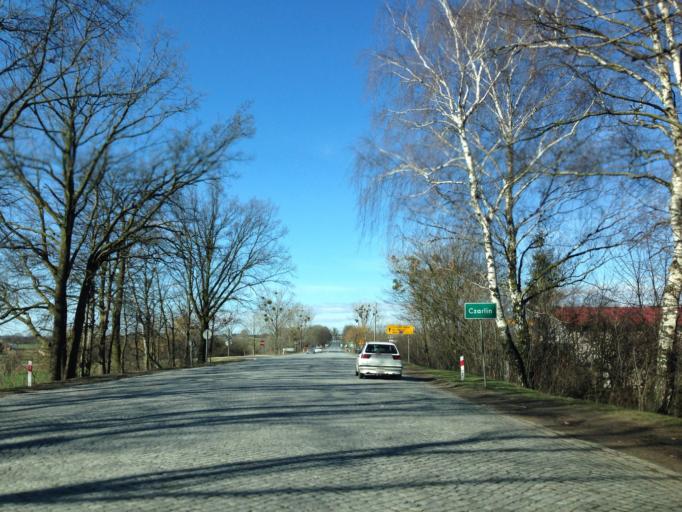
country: PL
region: Pomeranian Voivodeship
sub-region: Powiat tczewski
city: Subkowy
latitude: 54.0482
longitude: 18.7649
